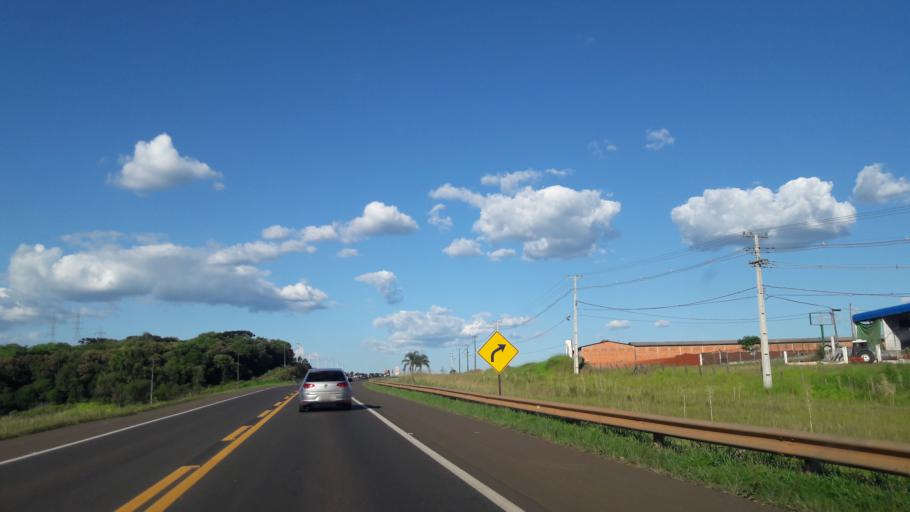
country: BR
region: Parana
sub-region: Guarapuava
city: Guarapuava
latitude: -25.3727
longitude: -51.5007
